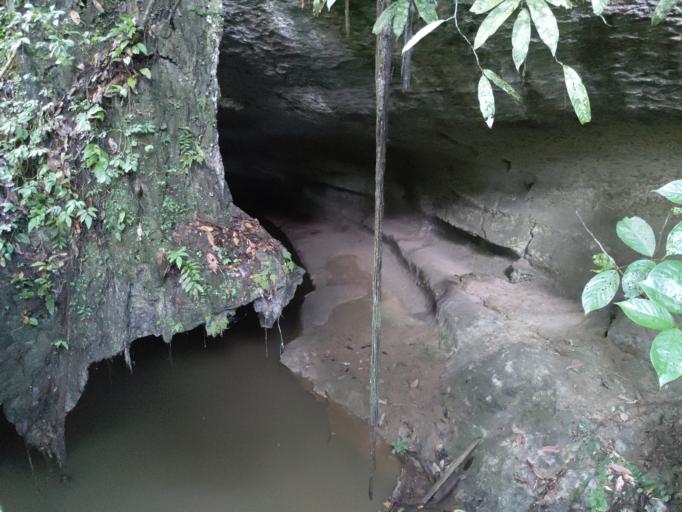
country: MY
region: Sarawak
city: Miri
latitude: 3.8225
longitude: 113.7756
